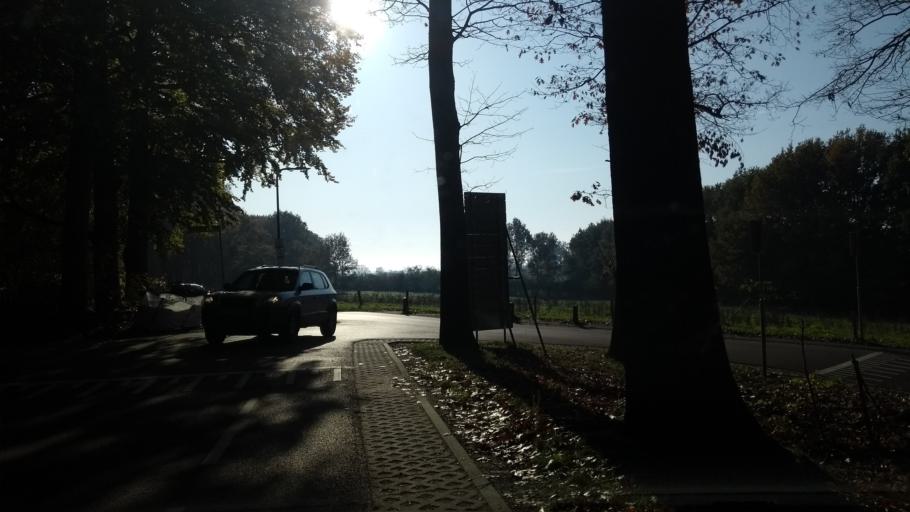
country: NL
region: Gelderland
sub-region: Gemeente Rheden
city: Rheden
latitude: 52.0165
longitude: 6.0281
